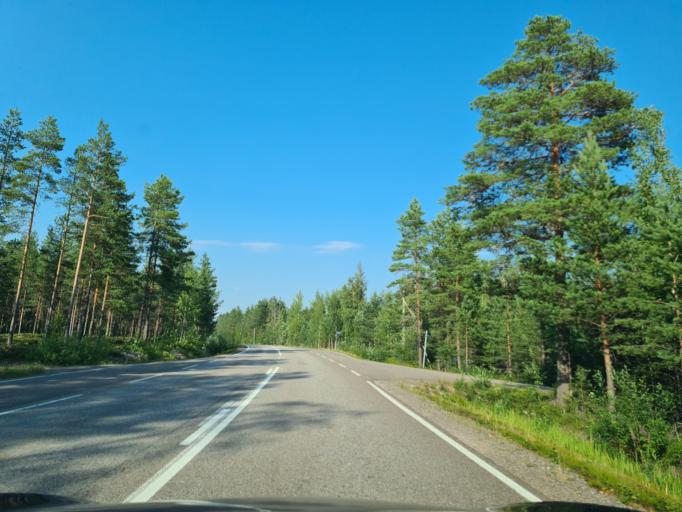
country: FI
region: Satakunta
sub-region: Pohjois-Satakunta
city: Karvia
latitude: 62.3183
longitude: 22.6659
